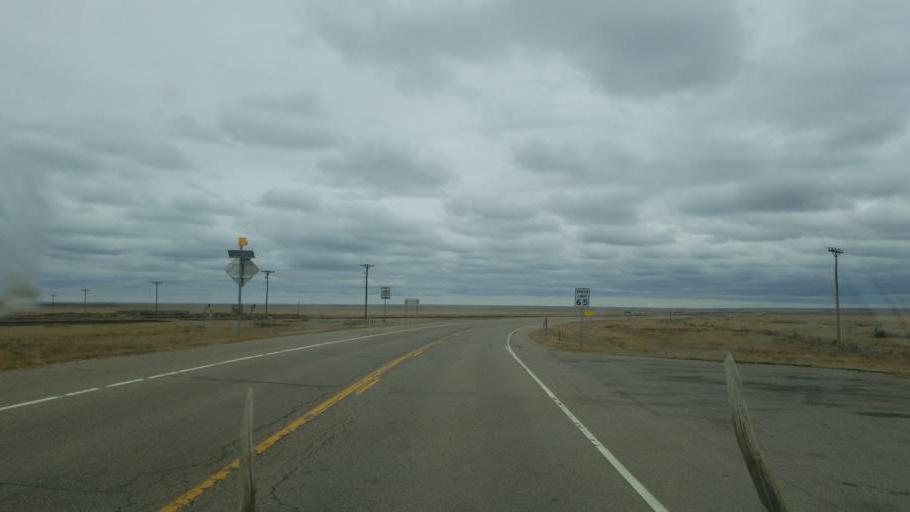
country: US
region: Colorado
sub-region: Kiowa County
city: Eads
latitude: 38.7646
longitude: -102.7777
